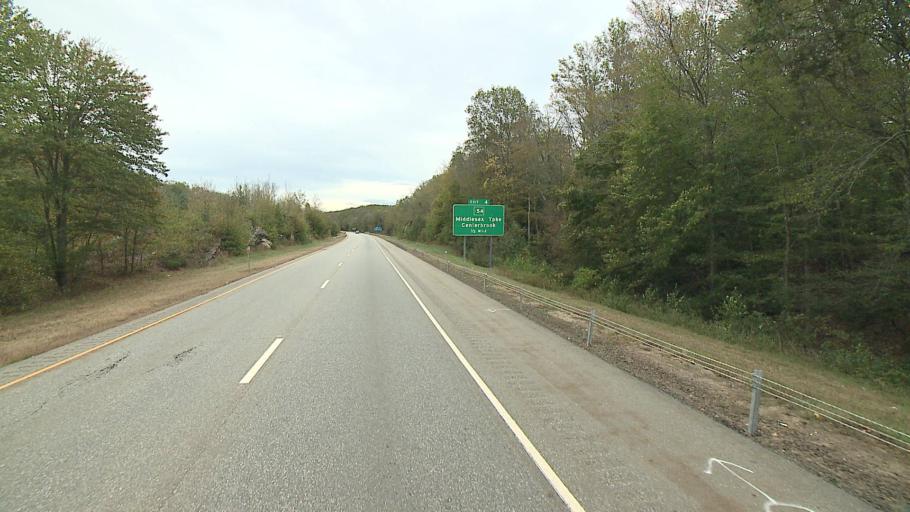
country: US
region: Connecticut
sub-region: Middlesex County
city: Deep River Center
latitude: 41.3699
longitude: -72.4343
